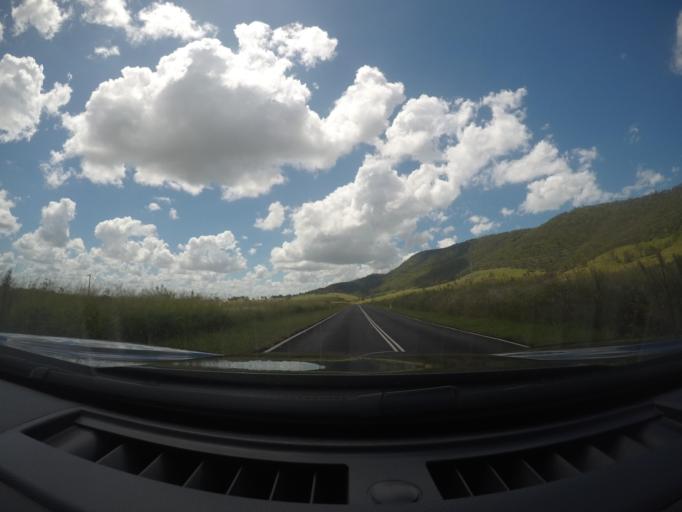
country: AU
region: Queensland
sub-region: Moreton Bay
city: Woodford
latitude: -27.1461
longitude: 152.5256
